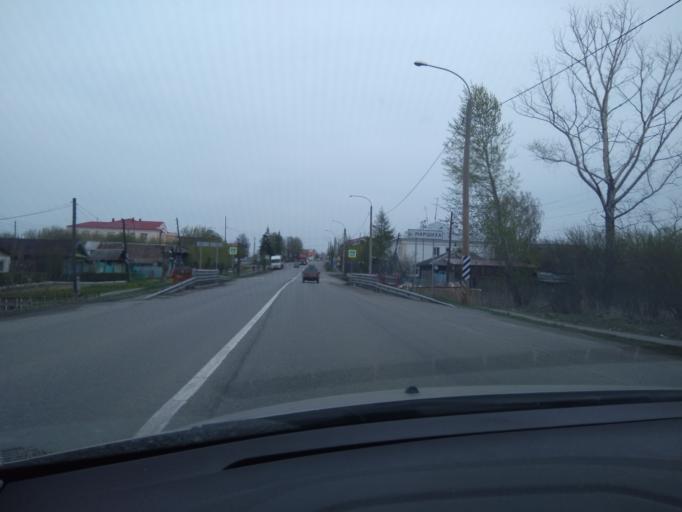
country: RU
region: Sverdlovsk
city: Beloyarskiy
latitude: 56.7592
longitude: 61.4096
